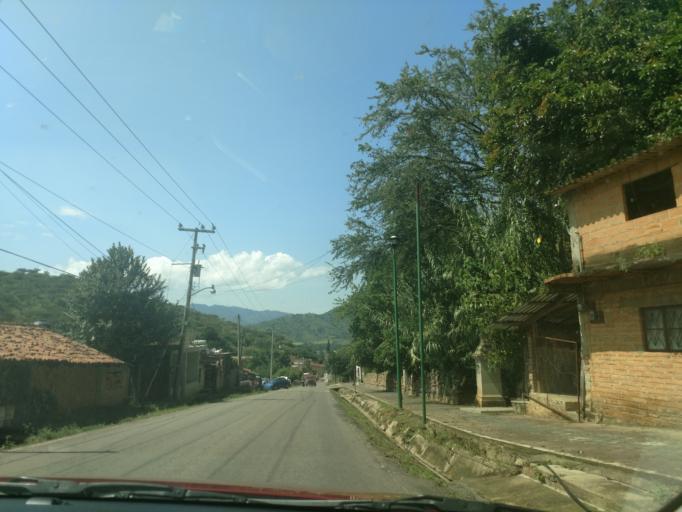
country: MX
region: Jalisco
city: Talpa de Allende
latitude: 20.3938
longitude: -104.8187
